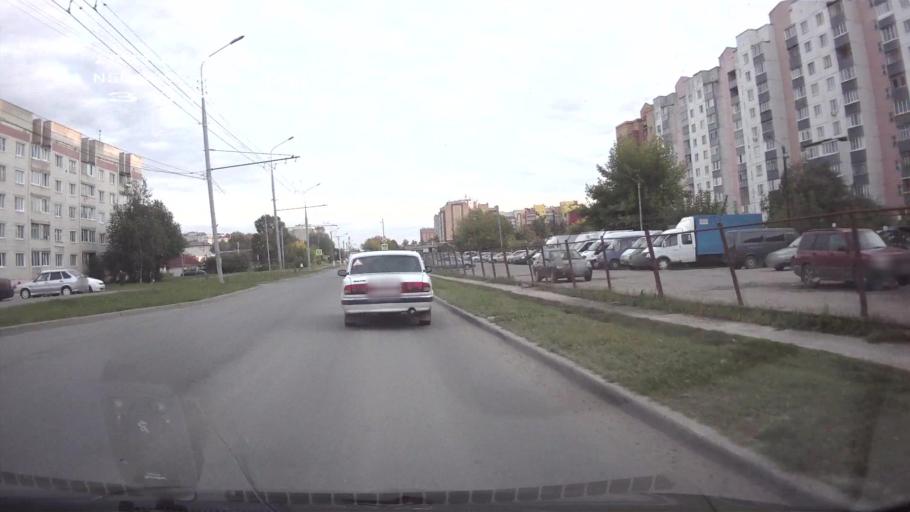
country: RU
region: Mariy-El
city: Yoshkar-Ola
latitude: 56.6502
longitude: 47.8552
